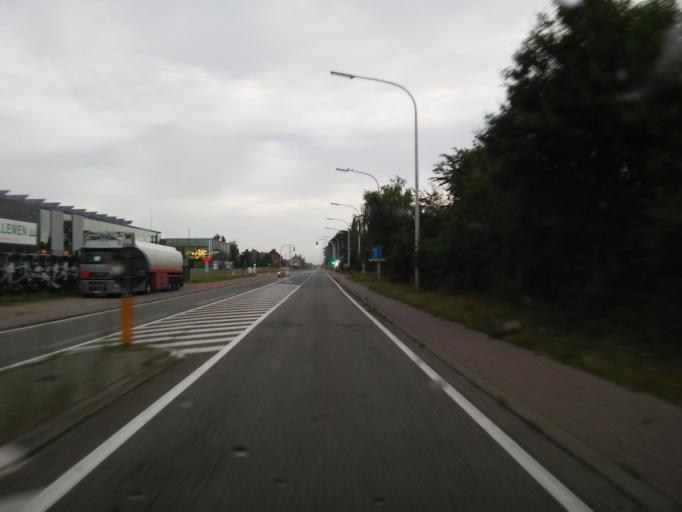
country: BE
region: Flanders
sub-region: Provincie Antwerpen
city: Kontich
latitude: 51.1015
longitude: 4.4512
